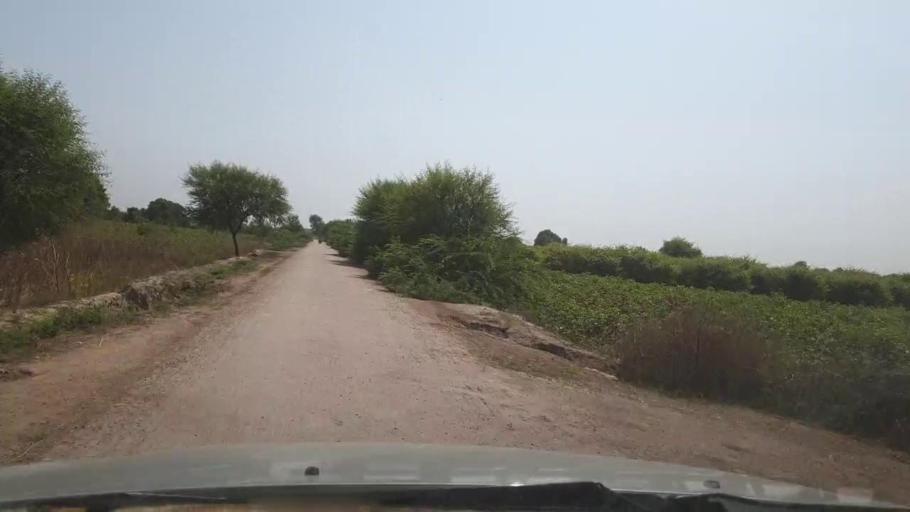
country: PK
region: Sindh
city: Tando Ghulam Ali
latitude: 25.1575
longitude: 68.8950
